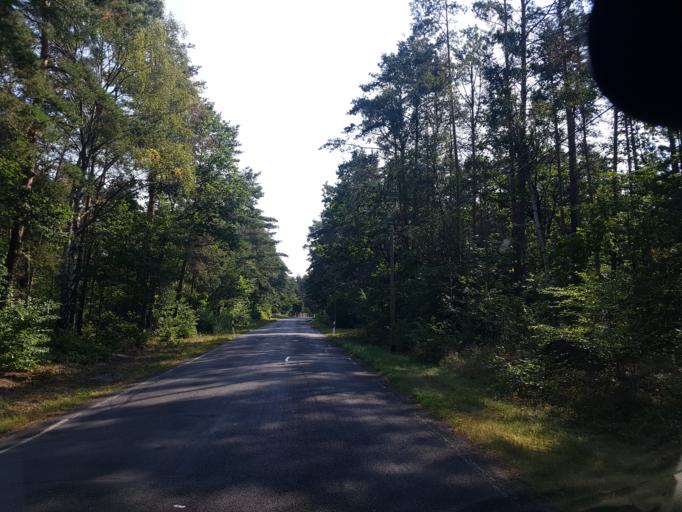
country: DE
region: Brandenburg
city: Lauchhammer
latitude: 51.5120
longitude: 13.7216
